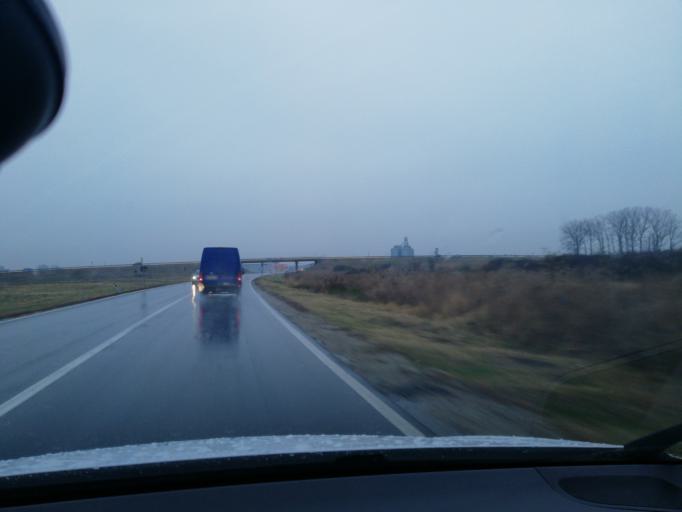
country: RS
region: Autonomna Pokrajina Vojvodina
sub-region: Sremski Okrug
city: Ruma
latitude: 45.0103
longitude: 19.8473
